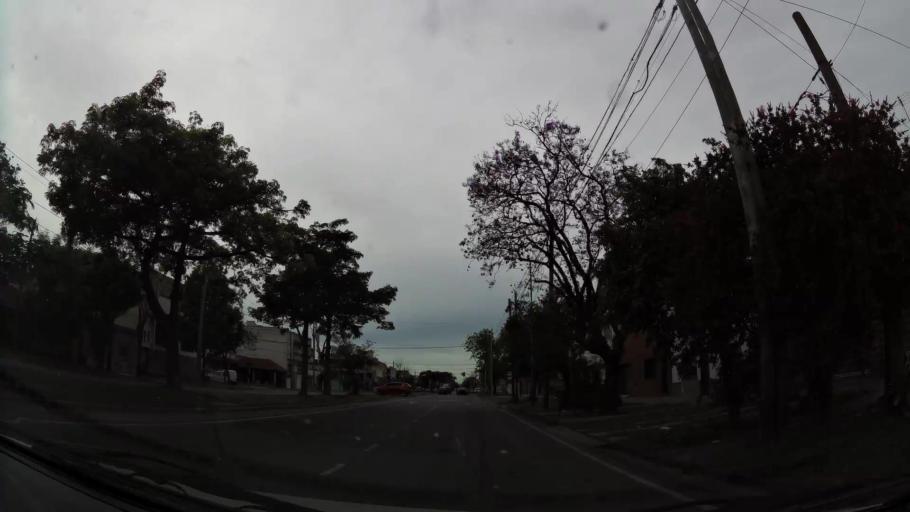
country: AR
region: Buenos Aires
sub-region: Partido de Avellaneda
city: Avellaneda
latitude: -34.6691
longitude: -58.3499
